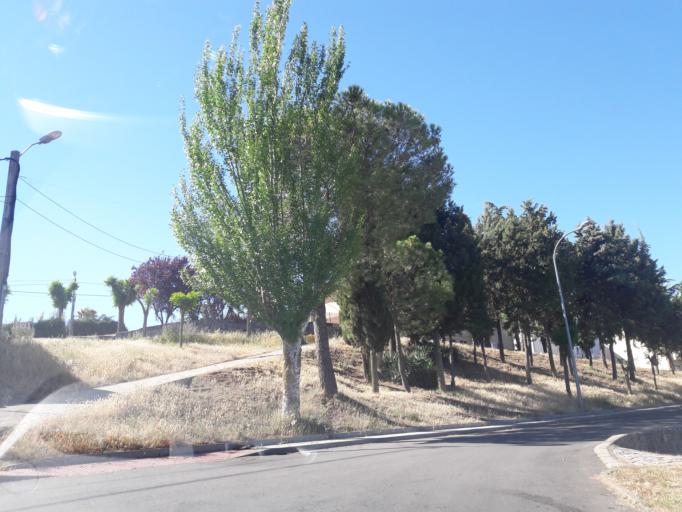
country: ES
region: Castille and Leon
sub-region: Provincia de Salamanca
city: Florida de Liebana
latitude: 41.0249
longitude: -5.7621
